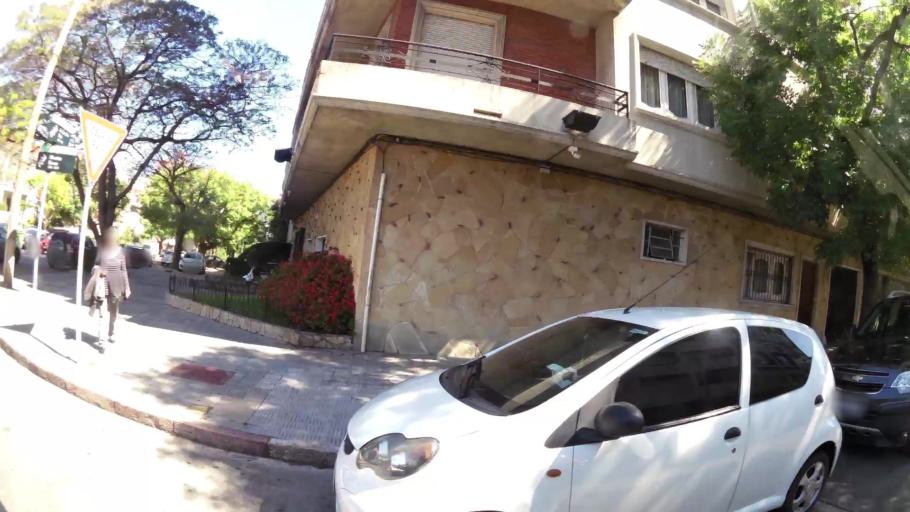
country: UY
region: Montevideo
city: Montevideo
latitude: -34.9040
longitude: -56.1558
